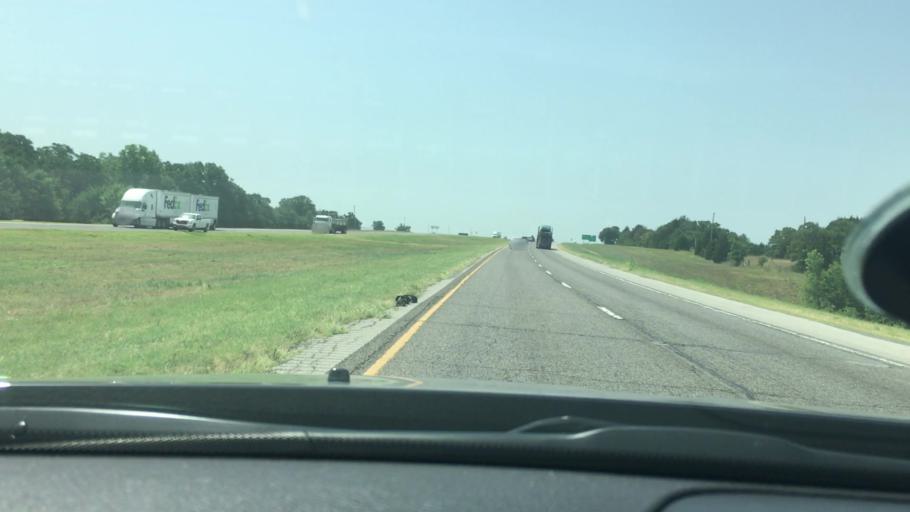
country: US
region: Oklahoma
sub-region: Garvin County
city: Wynnewood
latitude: 34.6347
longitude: -97.2178
